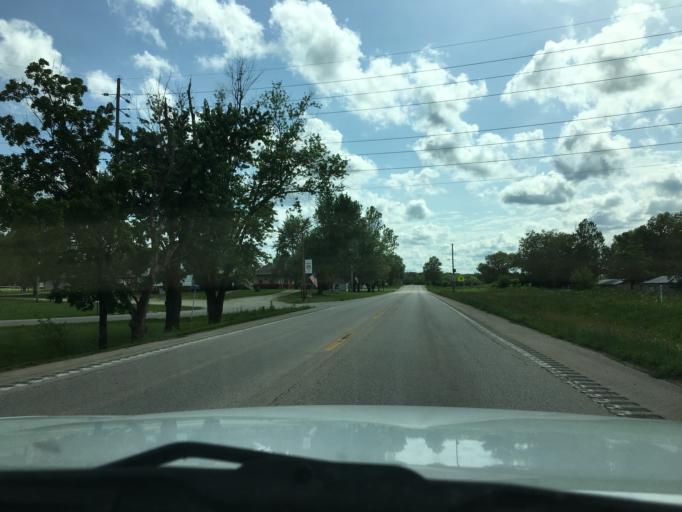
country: US
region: Missouri
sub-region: Franklin County
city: Gerald
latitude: 38.3983
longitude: -91.3358
